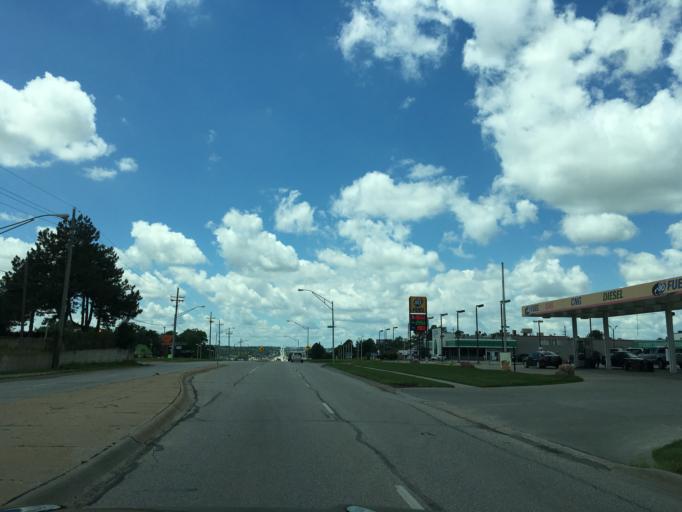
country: US
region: Nebraska
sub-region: Sarpy County
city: La Vista
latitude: 41.2126
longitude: -95.9965
